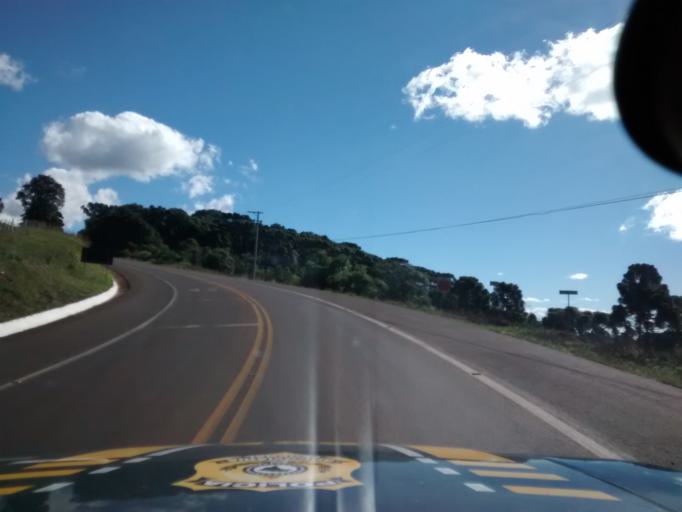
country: BR
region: Rio Grande do Sul
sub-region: Vacaria
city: Vacaria
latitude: -28.3238
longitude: -51.1924
